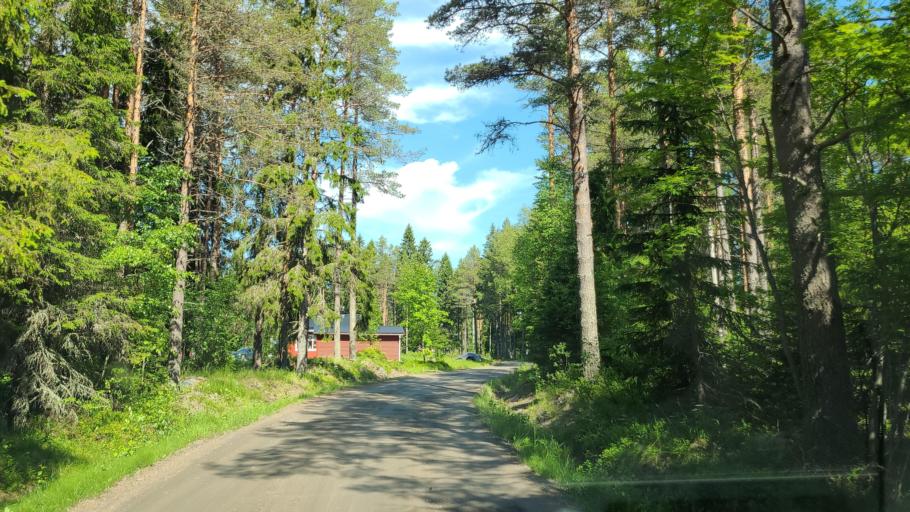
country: SE
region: Vaesterbotten
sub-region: Robertsfors Kommun
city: Robertsfors
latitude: 64.1427
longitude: 20.9606
